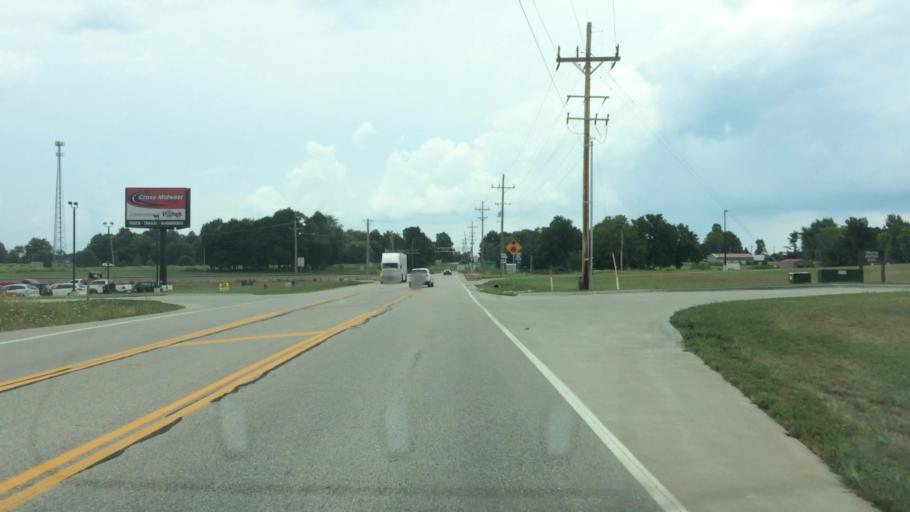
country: US
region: Missouri
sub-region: Greene County
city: Strafford
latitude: 37.2628
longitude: -93.1353
